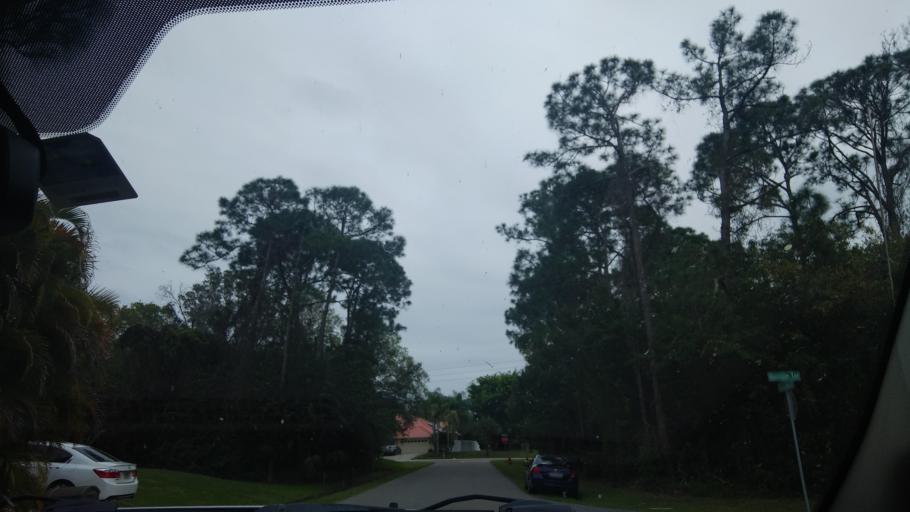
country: US
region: Florida
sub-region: Indian River County
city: Sebastian
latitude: 27.7582
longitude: -80.4906
